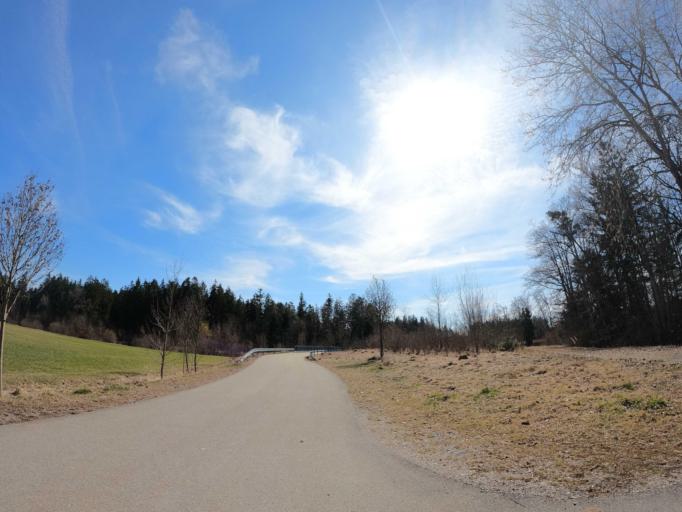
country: DE
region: Bavaria
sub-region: Upper Bavaria
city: Hohenkirchen-Siegertsbrunn
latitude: 48.0098
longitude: 11.7105
